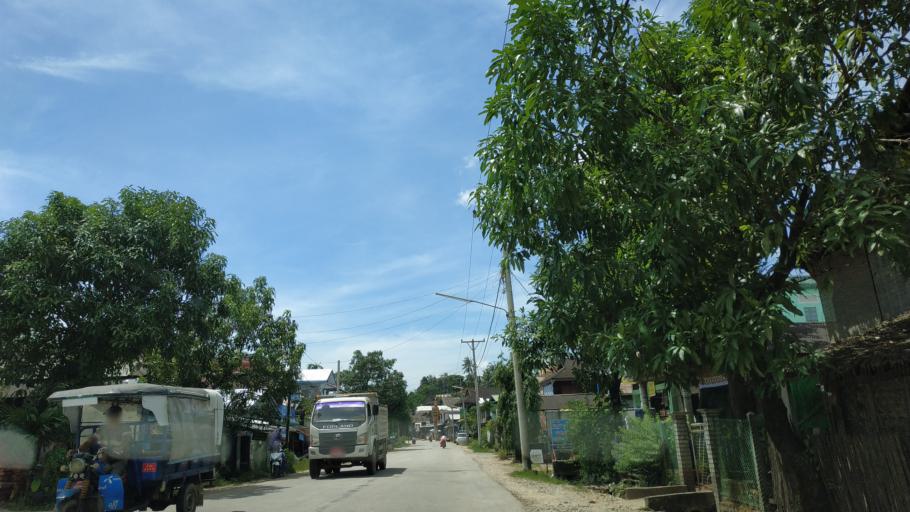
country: MM
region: Tanintharyi
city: Dawei
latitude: 14.1021
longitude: 98.1723
